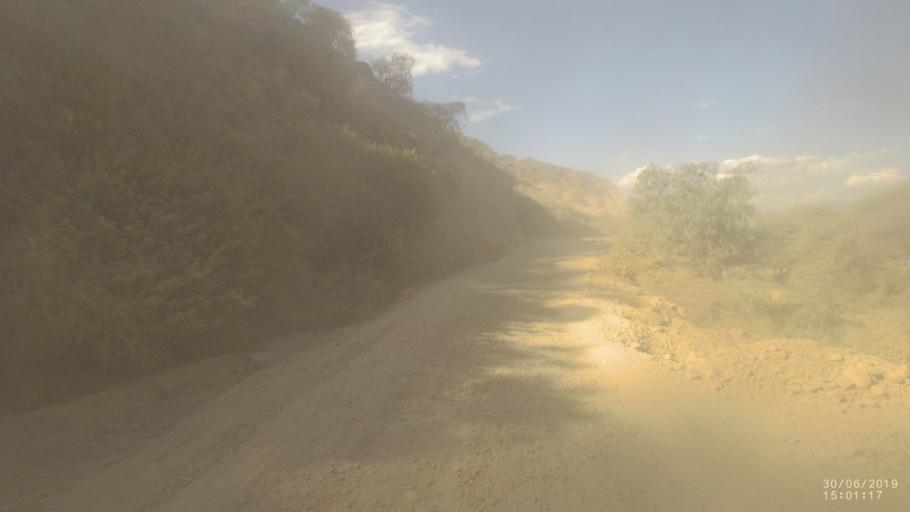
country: BO
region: Cochabamba
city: Irpa Irpa
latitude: -17.7332
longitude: -66.3372
